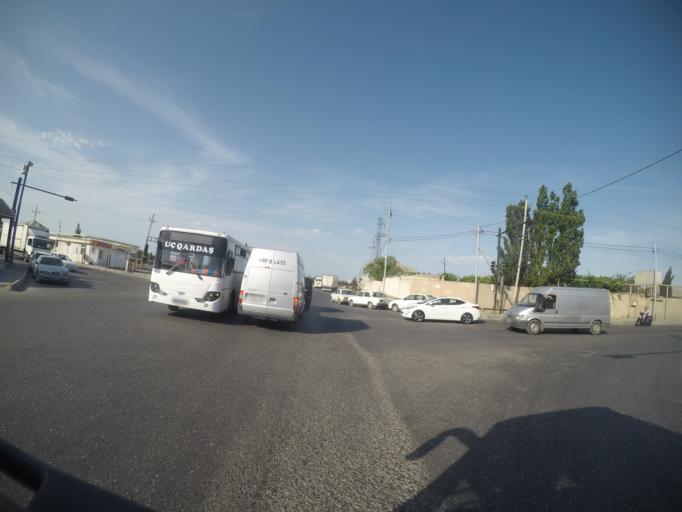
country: AZ
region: Baki
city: Bilajari
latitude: 40.4421
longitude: 49.7863
